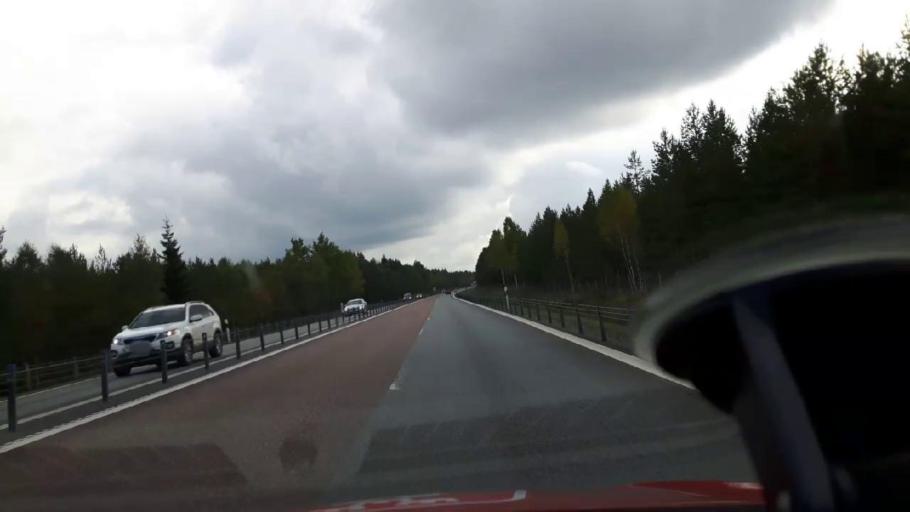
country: SE
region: Gaevleborg
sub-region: Gavle Kommun
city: Norrsundet
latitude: 60.8354
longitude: 17.0792
